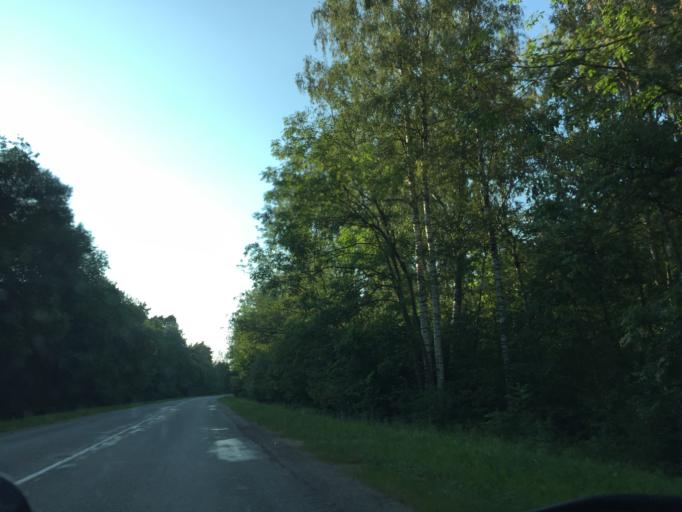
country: LV
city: Tervete
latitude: 56.4544
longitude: 23.4115
